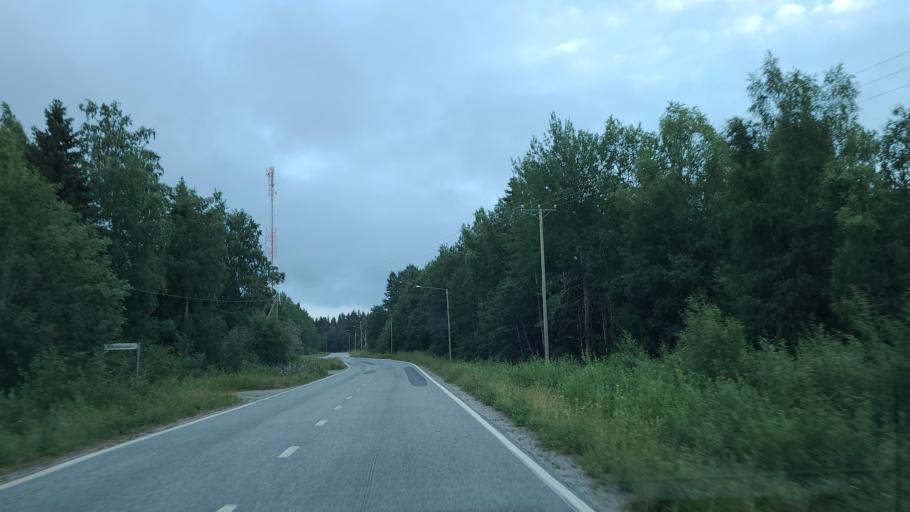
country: FI
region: Ostrobothnia
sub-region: Vaasa
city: Replot
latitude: 63.2885
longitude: 21.1148
